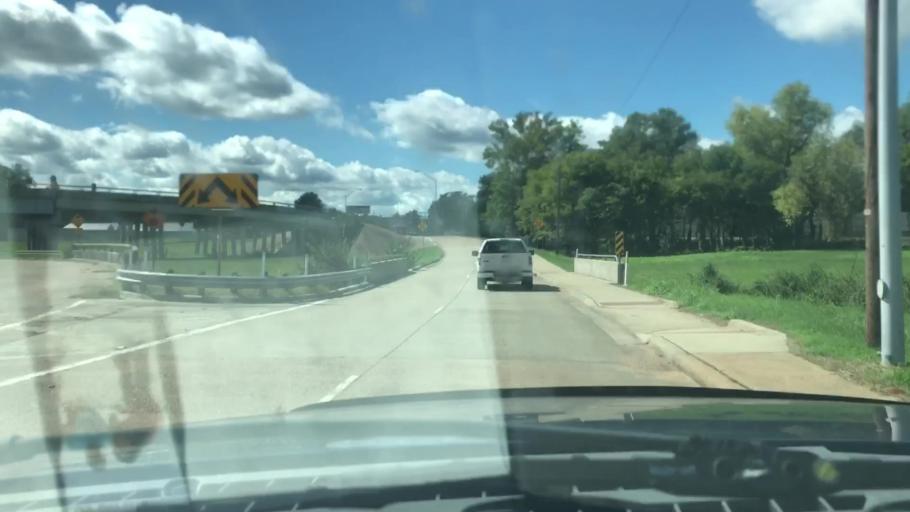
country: US
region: Texas
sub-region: Bowie County
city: Texarkana
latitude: 33.4206
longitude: -94.0504
